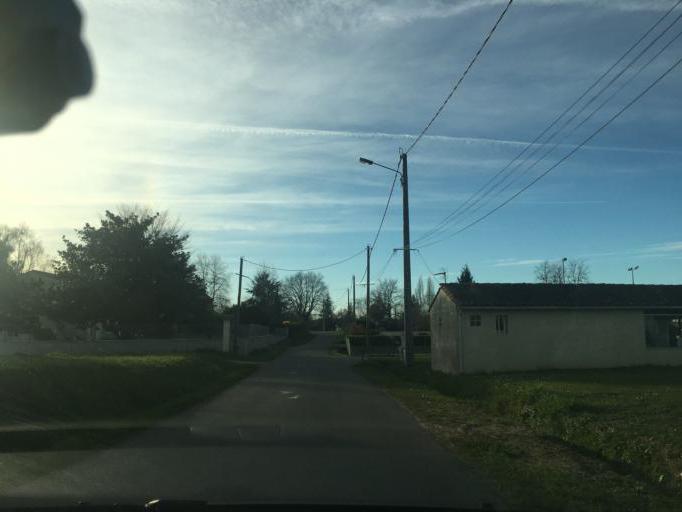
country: FR
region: Aquitaine
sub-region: Departement de la Gironde
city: Saint-Germain-du-Puch
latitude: 44.8624
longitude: -0.3230
